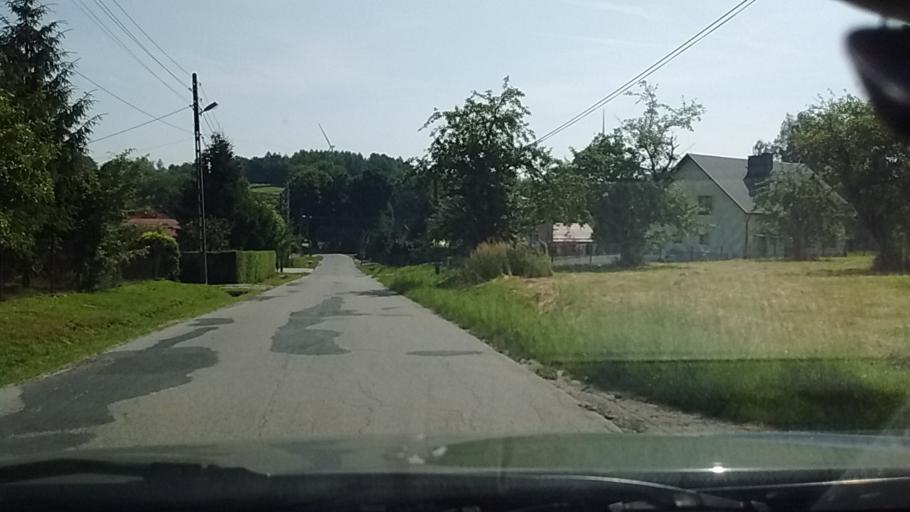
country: PL
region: Subcarpathian Voivodeship
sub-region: Powiat lancucki
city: Wysoka
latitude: 50.0481
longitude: 22.2692
